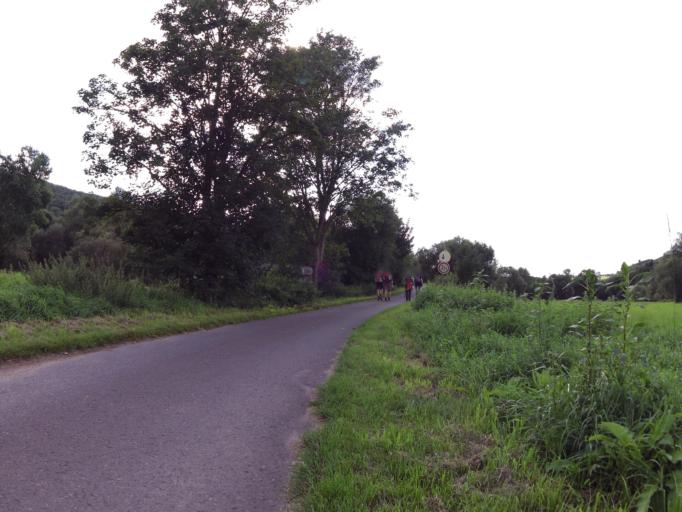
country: DE
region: Rheinland-Pfalz
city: Norheim
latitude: 49.8068
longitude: 7.8108
